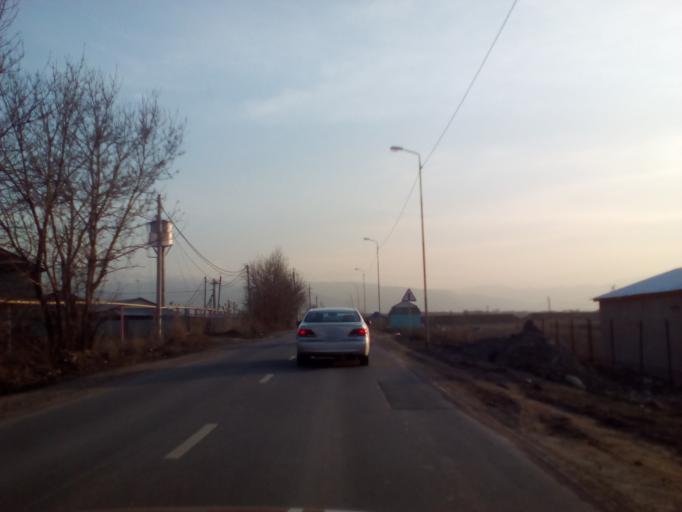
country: KZ
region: Almaty Oblysy
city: Burunday
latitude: 43.2370
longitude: 76.7429
